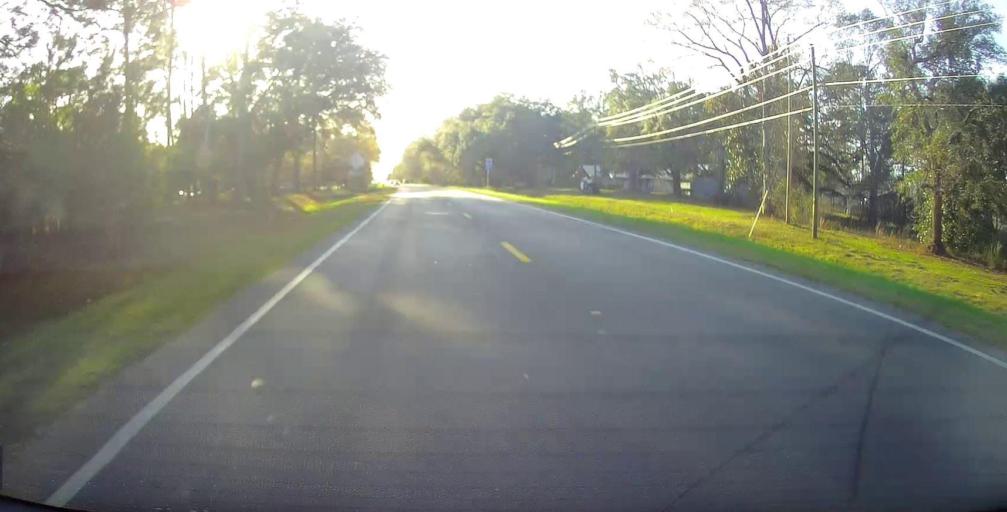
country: US
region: Georgia
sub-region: Evans County
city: Claxton
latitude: 32.1619
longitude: -81.8819
